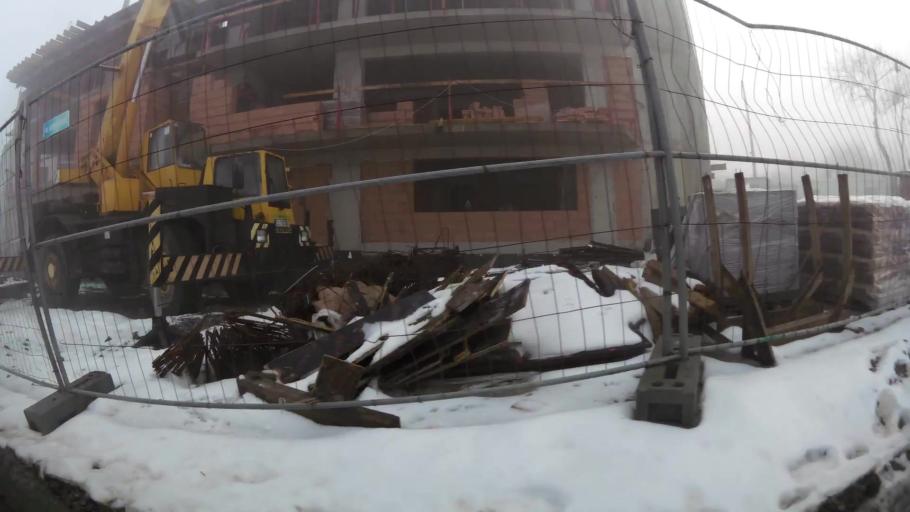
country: BG
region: Sofia-Capital
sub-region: Stolichna Obshtina
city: Sofia
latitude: 42.6553
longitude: 23.2603
